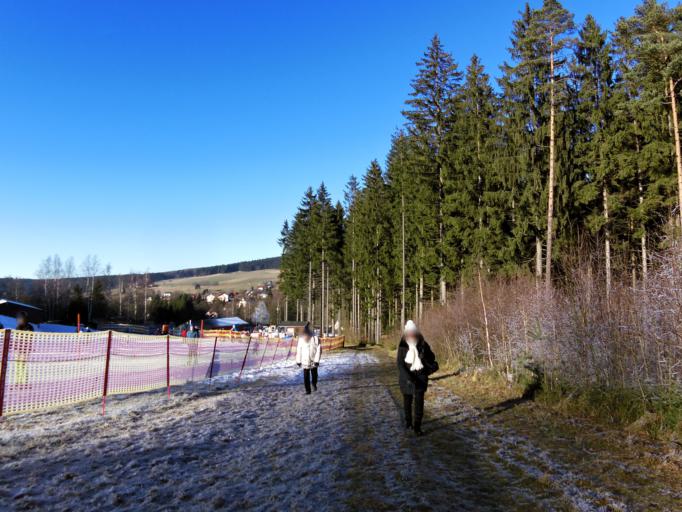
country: DE
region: Bavaria
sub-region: Upper Franconia
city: Bischofsgrun
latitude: 50.0499
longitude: 11.8137
